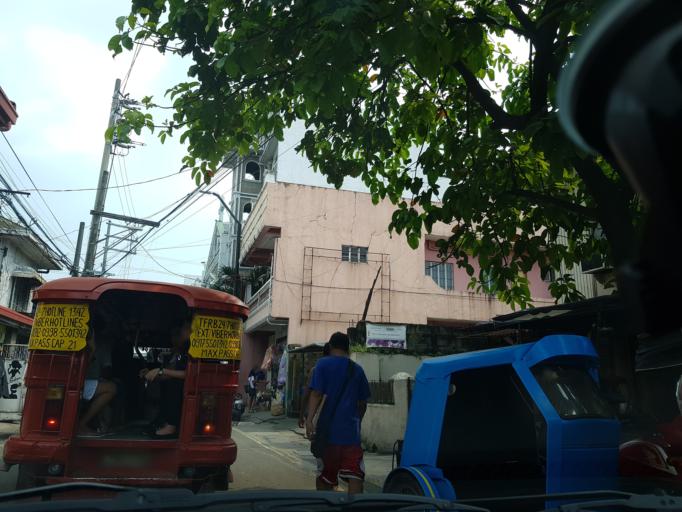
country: PH
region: Calabarzon
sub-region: Province of Rizal
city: Pateros
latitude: 14.5417
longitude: 121.0805
